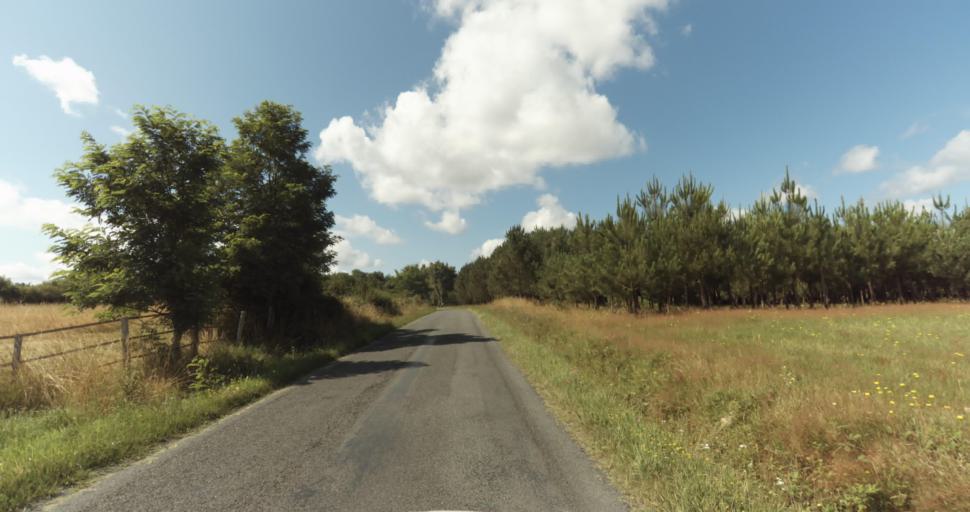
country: FR
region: Aquitaine
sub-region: Departement de la Gironde
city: Bazas
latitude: 44.4599
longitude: -0.2057
